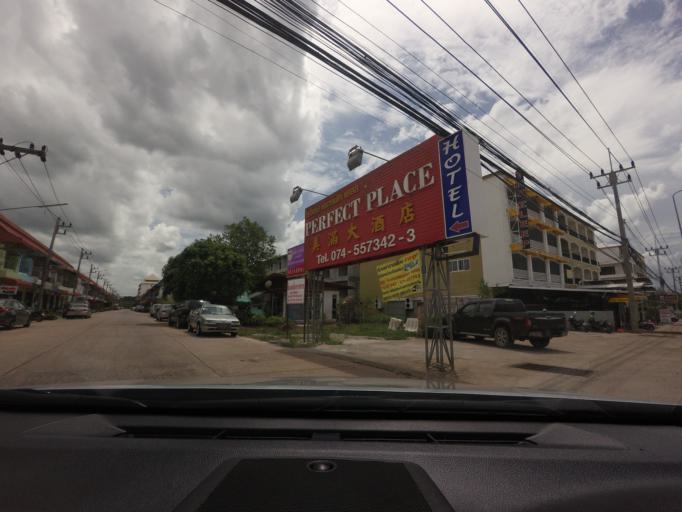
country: TH
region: Songkhla
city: Sadao
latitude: 6.5312
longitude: 100.4173
